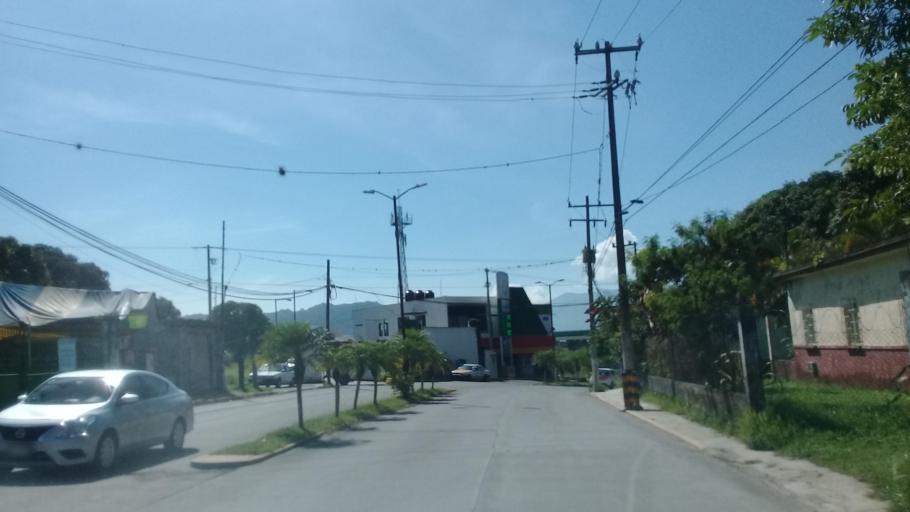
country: MX
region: Veracruz
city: Amatlan de los Reyes
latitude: 18.8541
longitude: -96.9123
